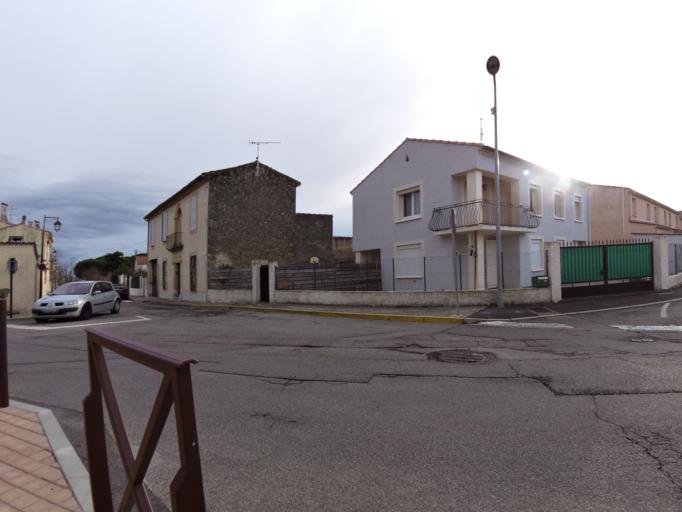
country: FR
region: Languedoc-Roussillon
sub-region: Departement du Gard
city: Vergeze
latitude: 43.7430
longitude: 4.2247
